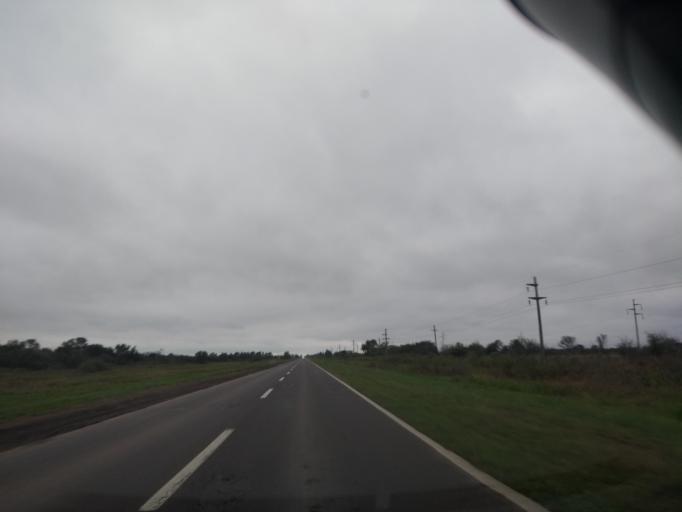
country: AR
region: Chaco
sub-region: Departamento de Quitilipi
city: Quitilipi
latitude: -26.8666
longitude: -60.2655
